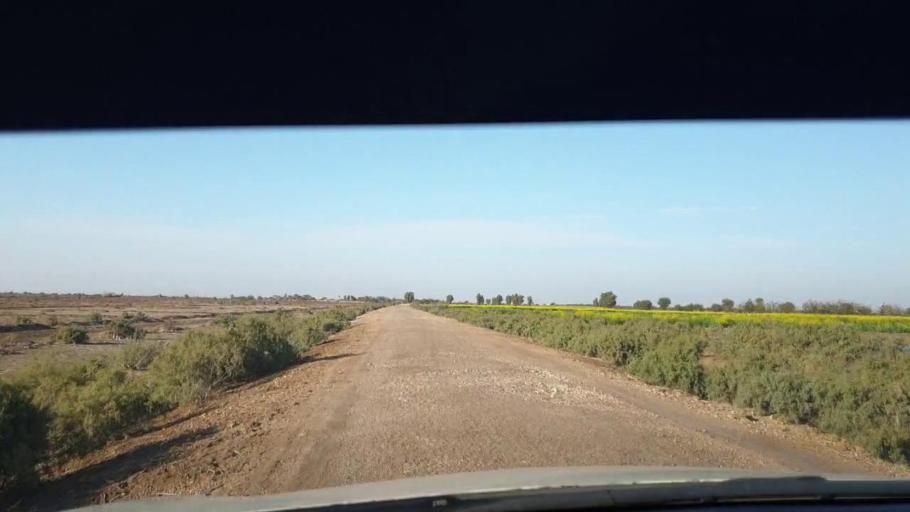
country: PK
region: Sindh
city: Berani
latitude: 25.8138
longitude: 68.9100
